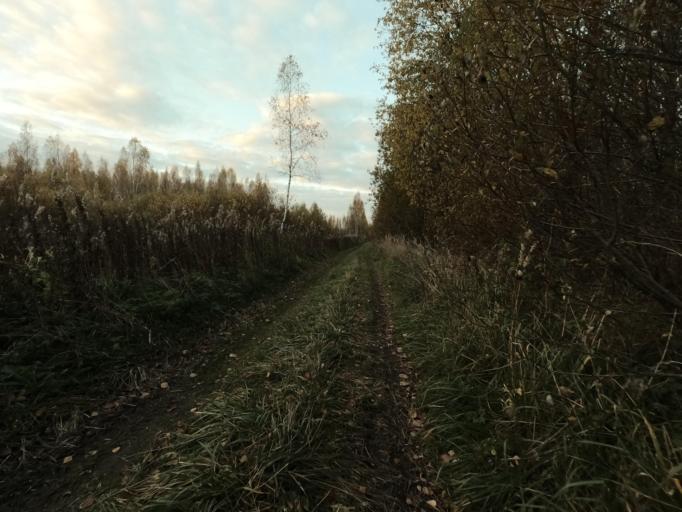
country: RU
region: Leningrad
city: Mga
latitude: 59.8184
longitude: 31.1780
